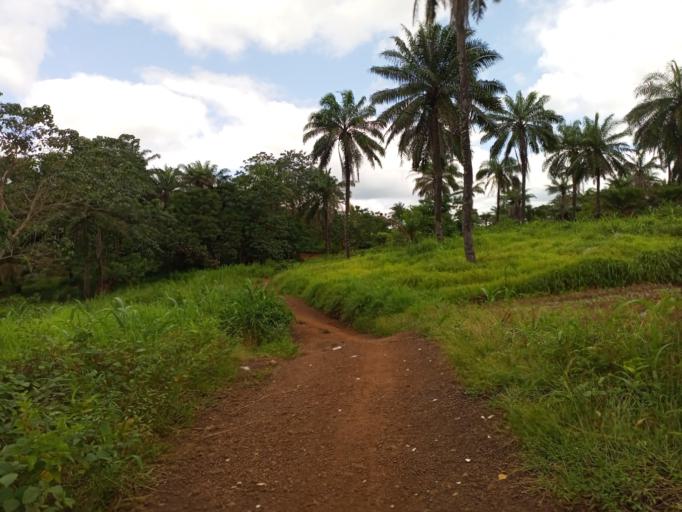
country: SL
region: Northern Province
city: Kamakwie
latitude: 9.4949
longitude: -12.2323
